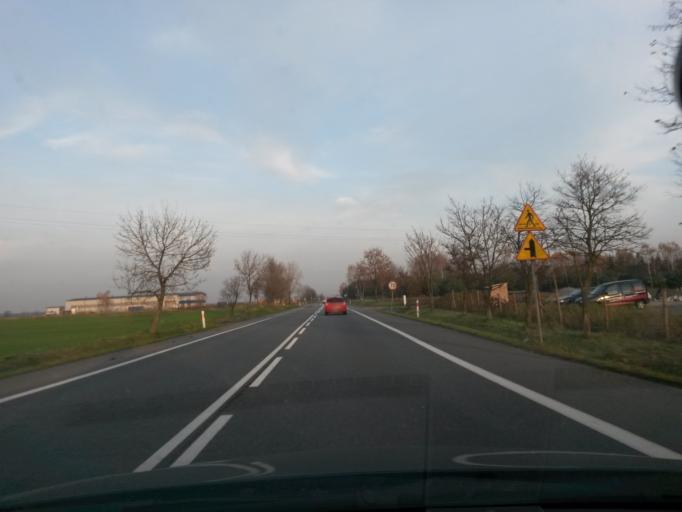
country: PL
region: Lodz Voivodeship
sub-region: Powiat wielunski
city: Wierzchlas
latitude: 51.2348
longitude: 18.6501
